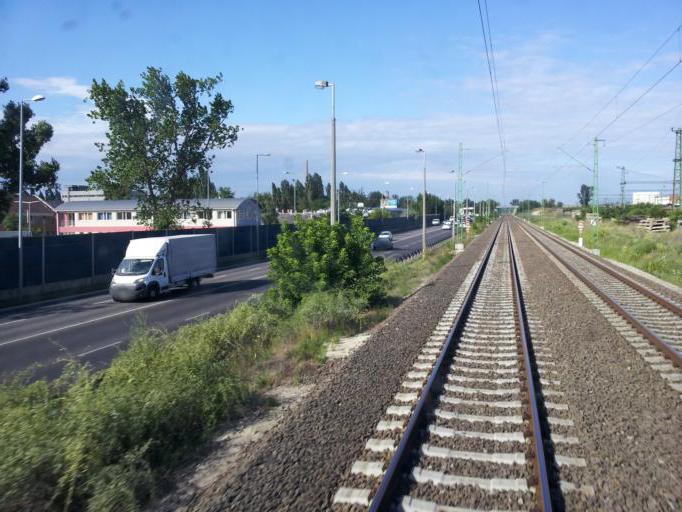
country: HU
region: Budapest
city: Budapest XXII. keruelet
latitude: 47.4120
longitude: 19.0369
